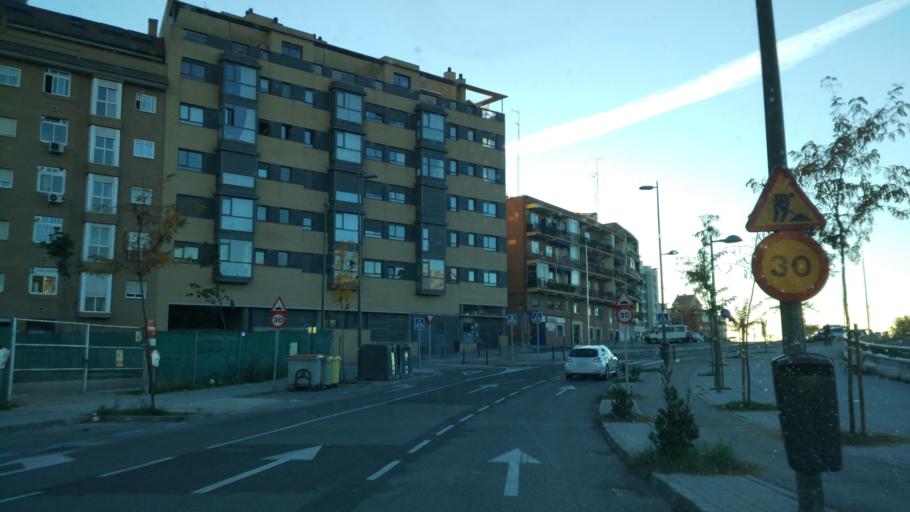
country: ES
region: Madrid
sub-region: Provincia de Madrid
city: Tetuan de las Victorias
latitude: 40.4703
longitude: -3.7029
